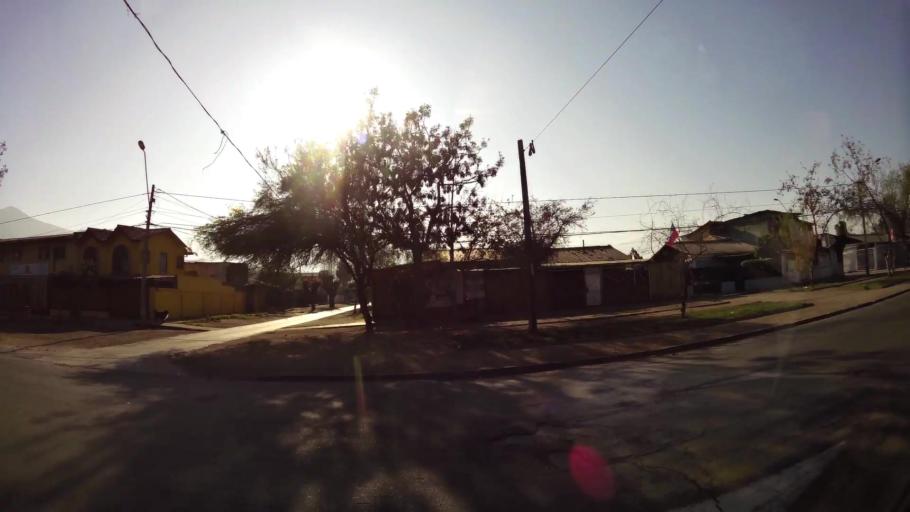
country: CL
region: Santiago Metropolitan
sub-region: Provincia de Santiago
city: Santiago
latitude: -33.3776
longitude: -70.6613
